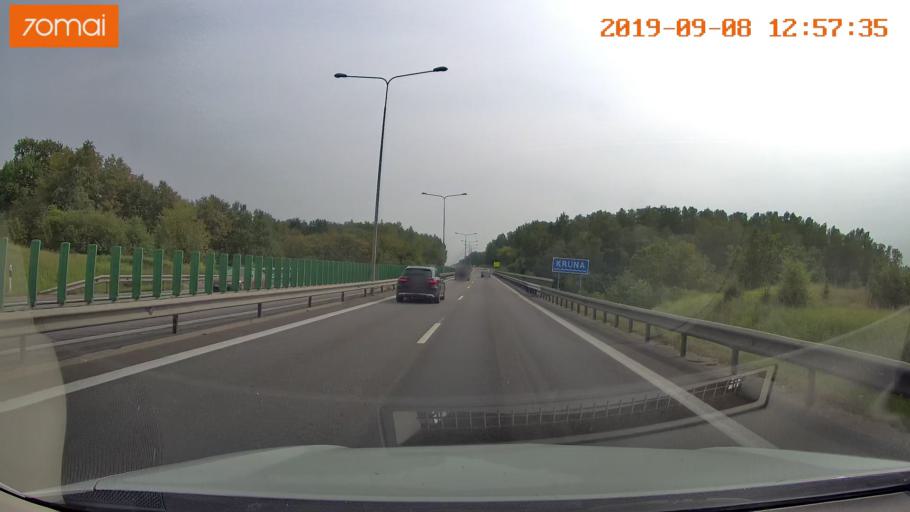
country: LT
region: Kauno apskritis
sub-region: Kauno rajonas
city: Karmelava
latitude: 54.9135
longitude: 24.0998
